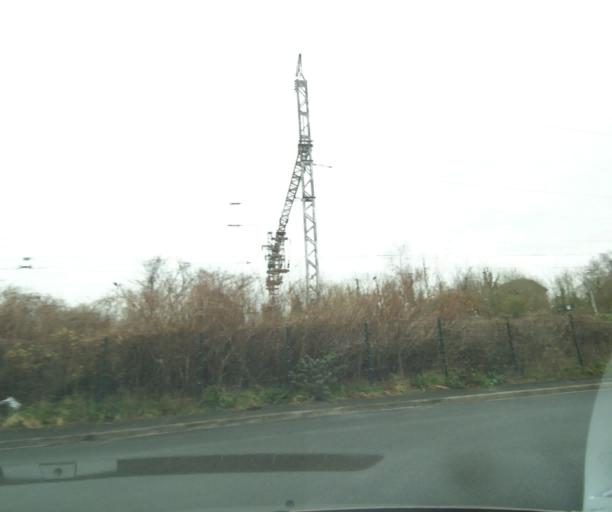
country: FR
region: Picardie
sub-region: Departement de l'Oise
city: Noyon
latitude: 49.5763
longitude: 3.0044
